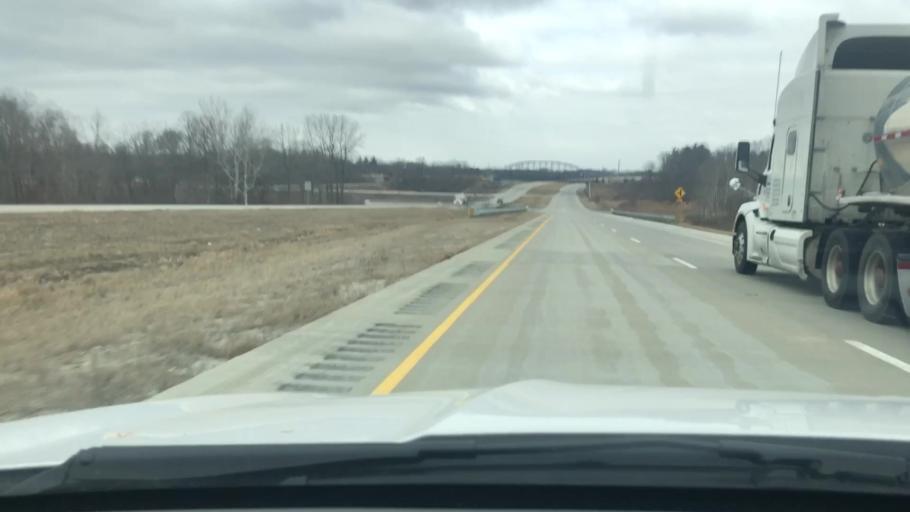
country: US
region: Indiana
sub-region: Carroll County
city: Delphi
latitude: 40.5891
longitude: -86.6521
